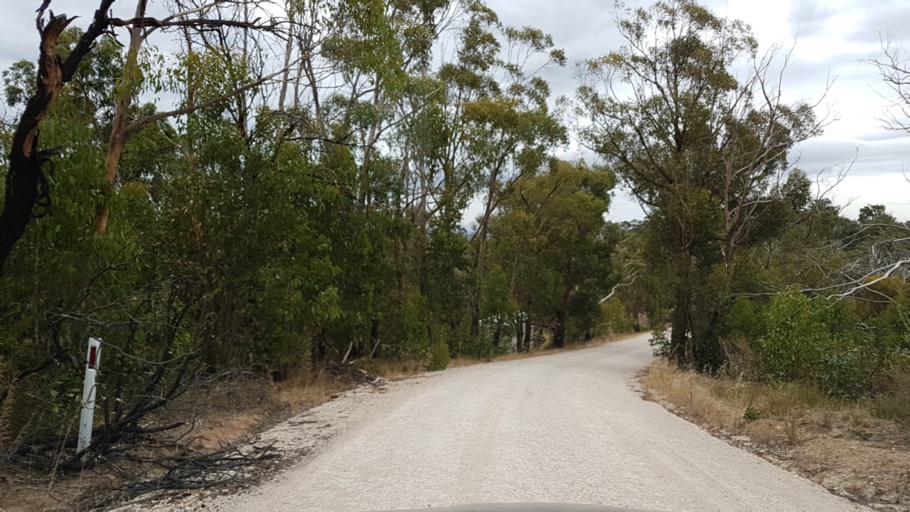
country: AU
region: South Australia
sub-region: Tea Tree Gully
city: Golden Grove
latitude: -34.7802
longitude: 138.8130
